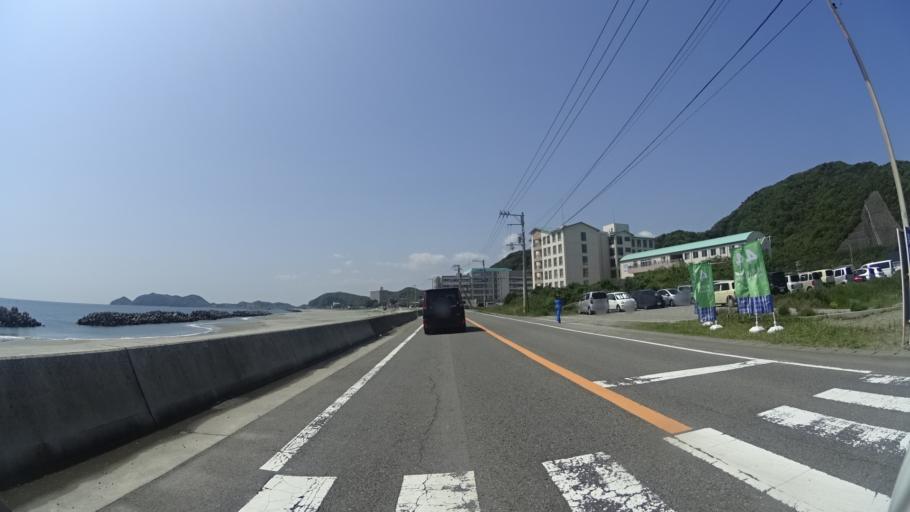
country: JP
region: Tokushima
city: Narutocho-mitsuishi
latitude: 34.2075
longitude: 134.6270
